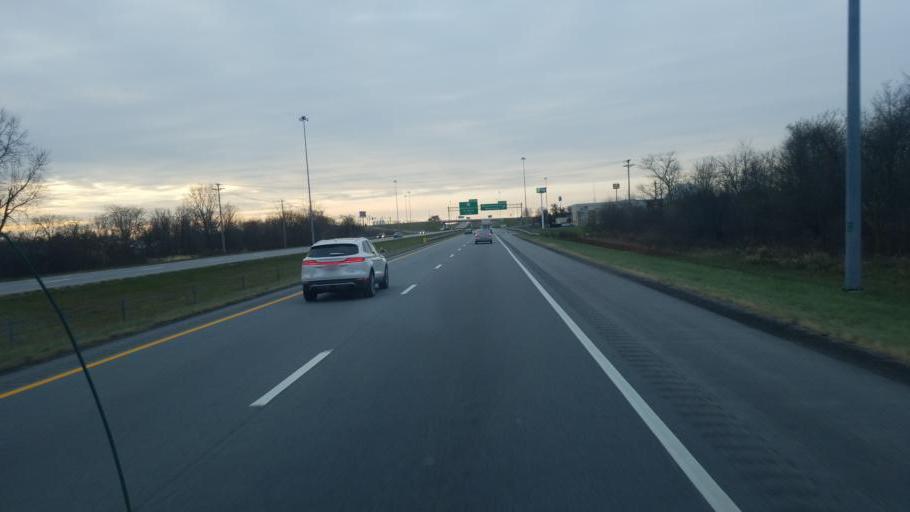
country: US
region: Ohio
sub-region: Auglaize County
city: Wapakoneta
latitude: 40.5665
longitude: -84.1702
